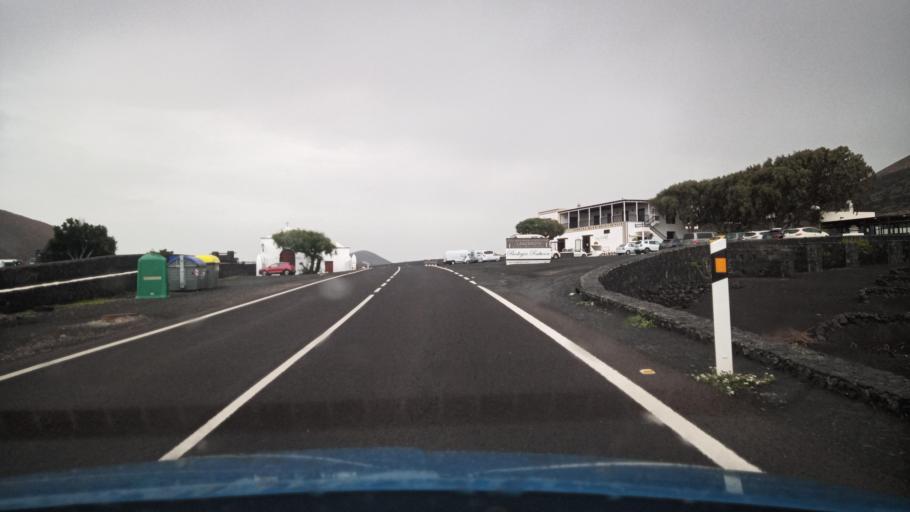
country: ES
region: Canary Islands
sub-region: Provincia de Las Palmas
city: Yaiza
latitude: 28.9684
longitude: -13.7150
